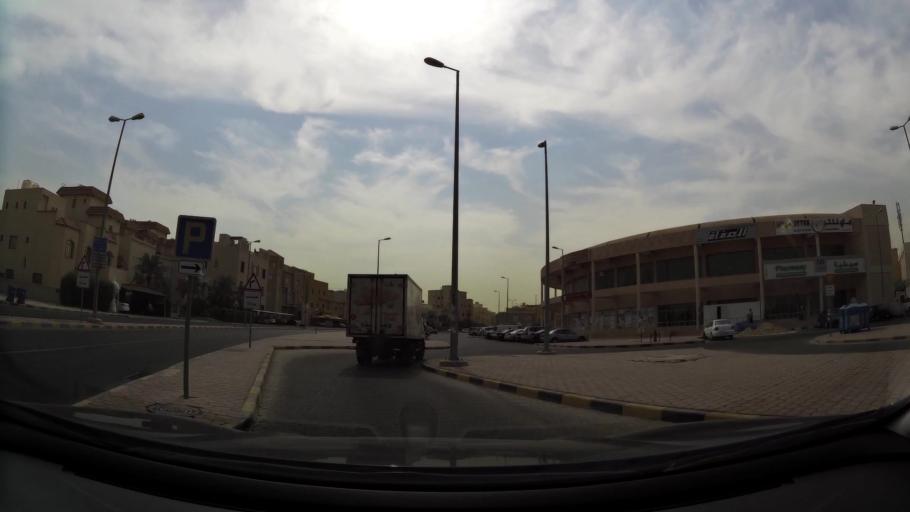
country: KW
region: Mubarak al Kabir
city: Sabah as Salim
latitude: 29.2708
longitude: 48.0343
